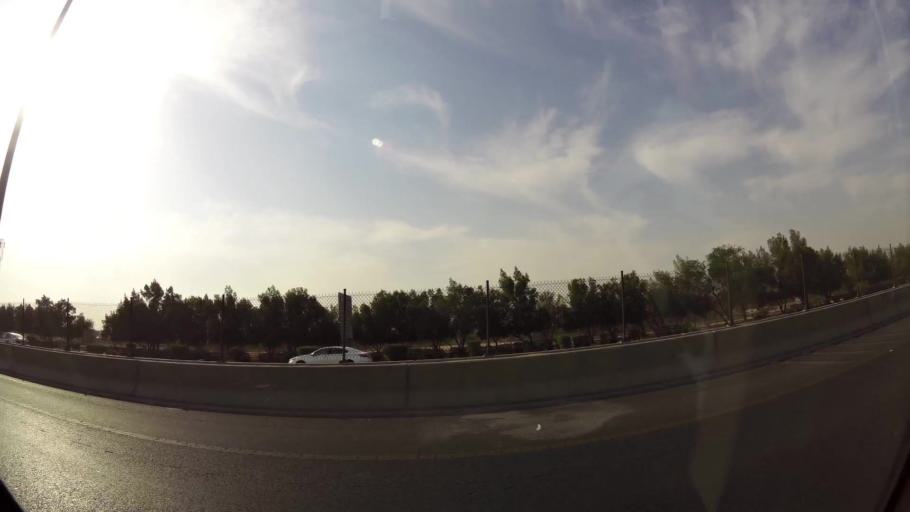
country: KW
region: Mubarak al Kabir
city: Sabah as Salim
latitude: 29.2653
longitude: 48.0312
